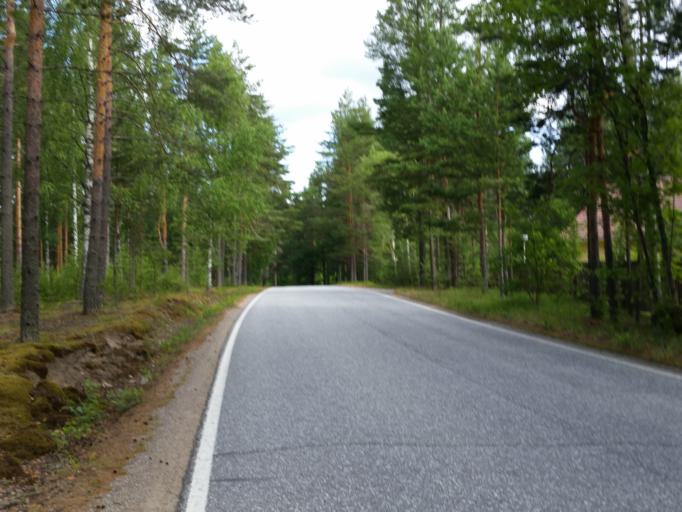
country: FI
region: Southern Savonia
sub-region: Savonlinna
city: Sulkava
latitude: 61.7693
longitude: 28.4345
